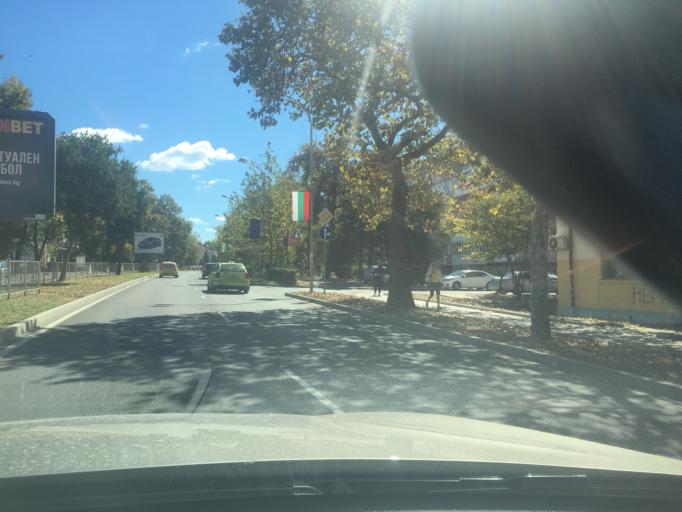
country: BG
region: Burgas
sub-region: Obshtina Burgas
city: Burgas
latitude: 42.5097
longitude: 27.4674
